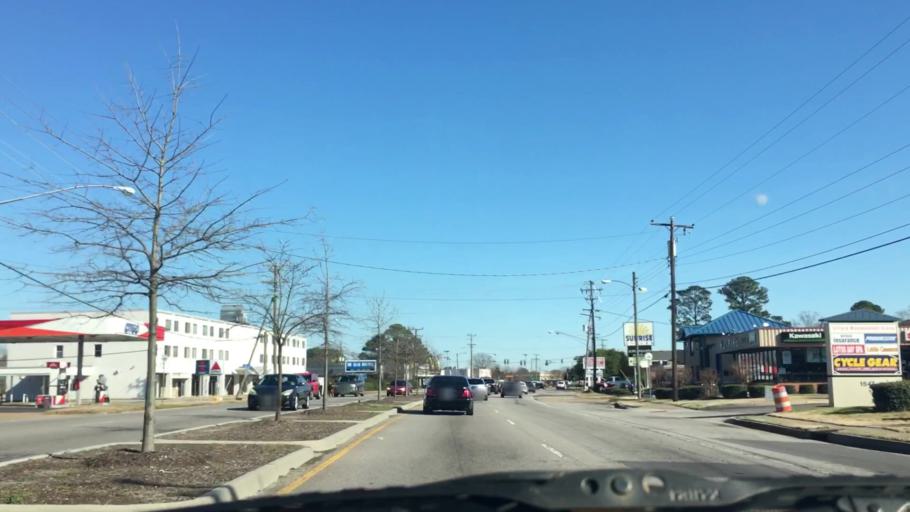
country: US
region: Virginia
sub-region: City of Norfolk
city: Norfolk
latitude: 36.9166
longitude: -76.2323
